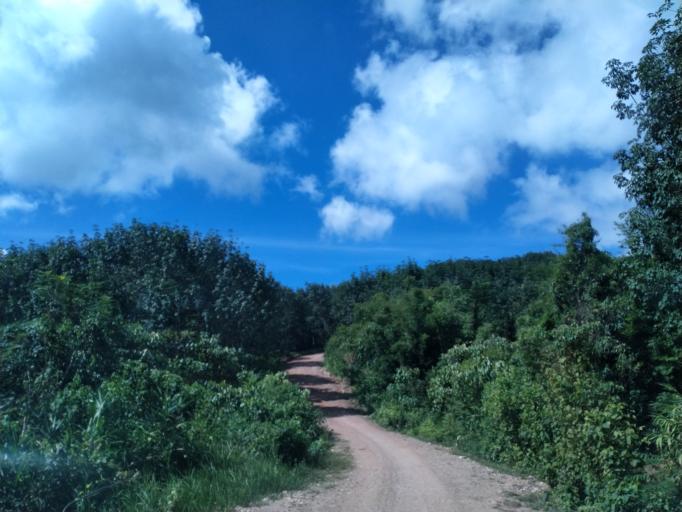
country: TH
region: Nong Khai
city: Rattanawapi
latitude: 18.6385
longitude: 102.9445
